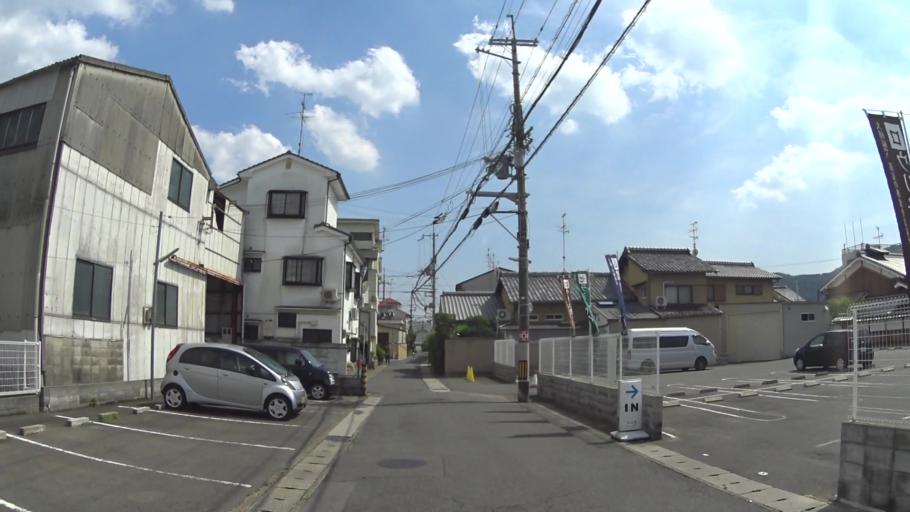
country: JP
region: Kyoto
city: Muko
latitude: 35.0137
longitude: 135.6938
